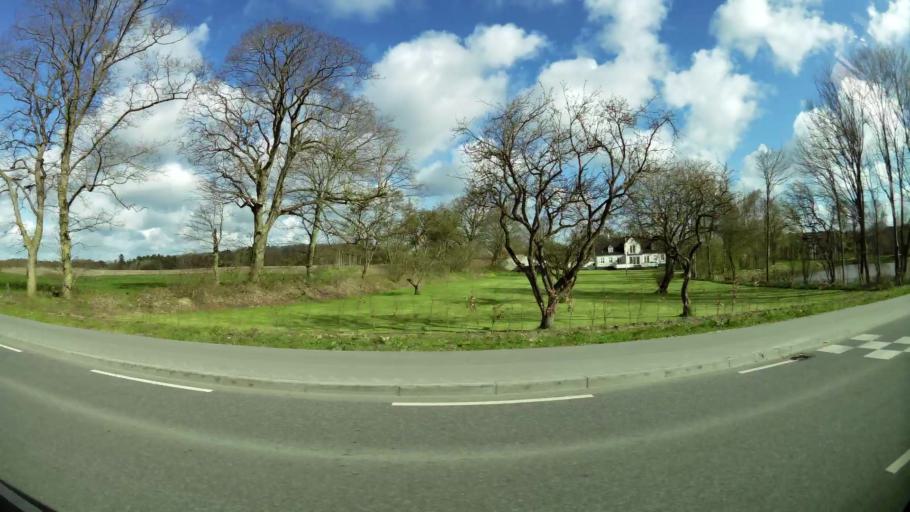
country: DK
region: North Denmark
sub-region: Mariagerfjord Kommune
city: Hobro
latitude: 56.6269
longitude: 9.8616
